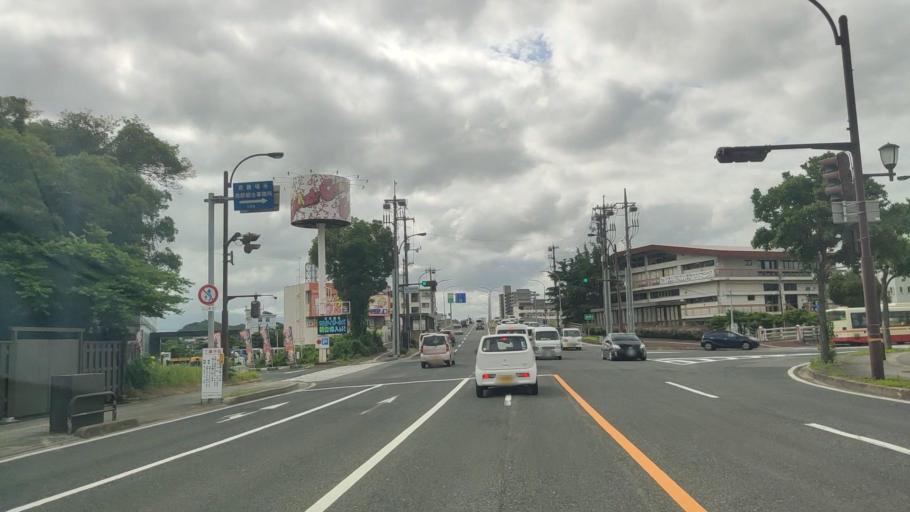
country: JP
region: Tottori
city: Yonago
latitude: 35.4294
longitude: 133.3385
